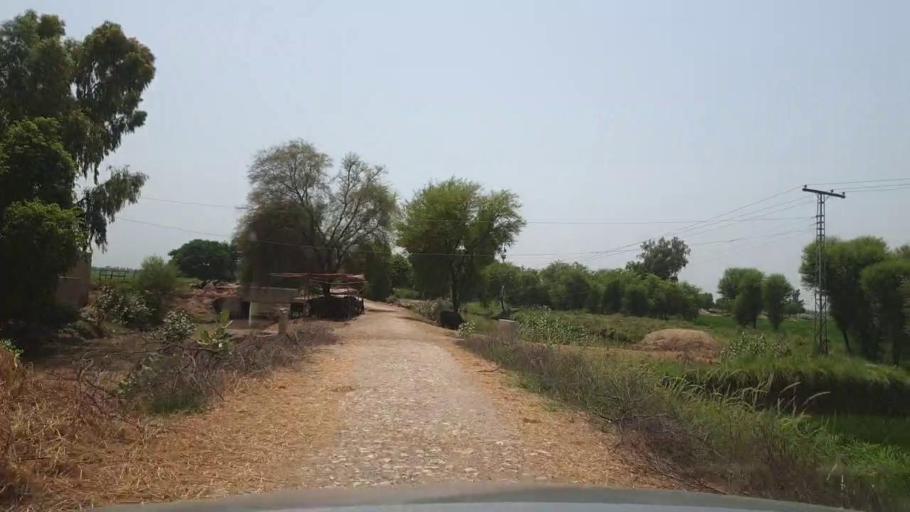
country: PK
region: Sindh
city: Ratodero
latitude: 27.7928
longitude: 68.3413
